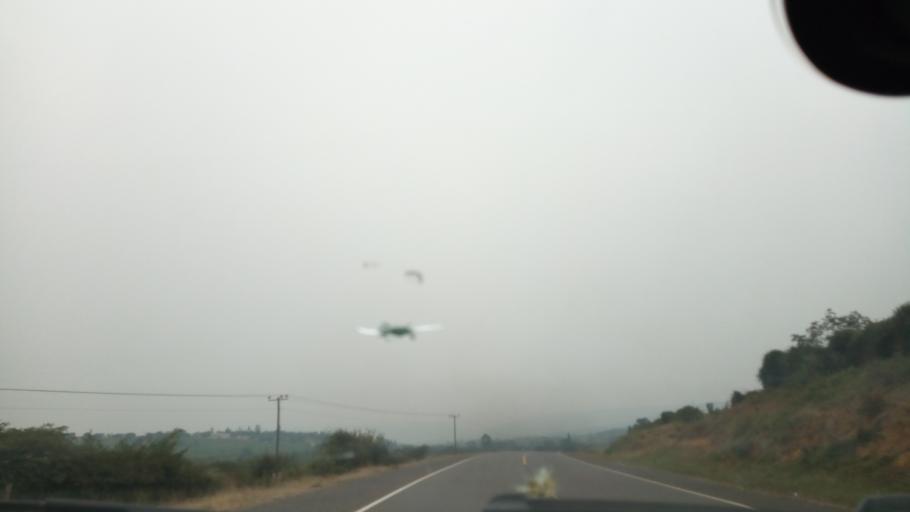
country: UG
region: Western Region
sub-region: Mbarara District
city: Mbarara
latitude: -0.7177
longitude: 30.7249
